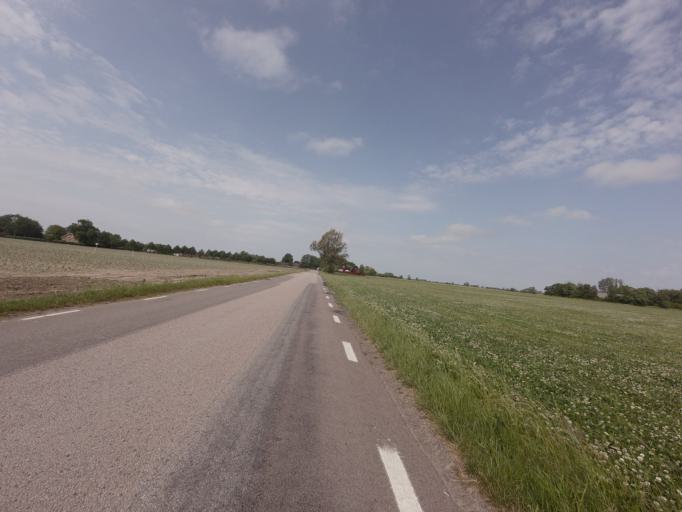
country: SE
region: Skane
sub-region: Hoganas Kommun
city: Hoganas
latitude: 56.1874
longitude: 12.6446
